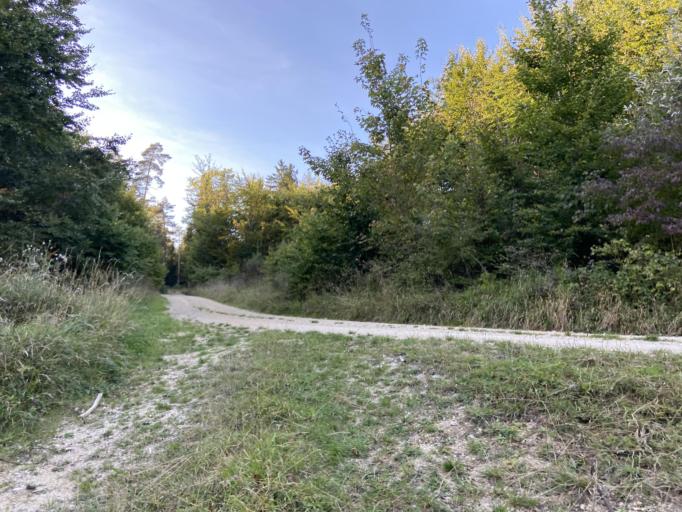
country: DE
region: Baden-Wuerttemberg
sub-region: Tuebingen Region
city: Bingen
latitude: 48.1324
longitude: 9.2843
